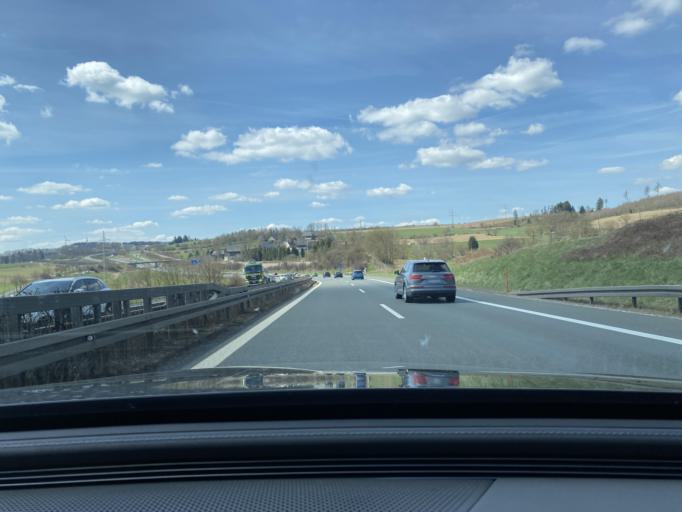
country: DE
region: Bavaria
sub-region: Upper Franconia
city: Leupoldsgrun
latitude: 50.3317
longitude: 11.8062
